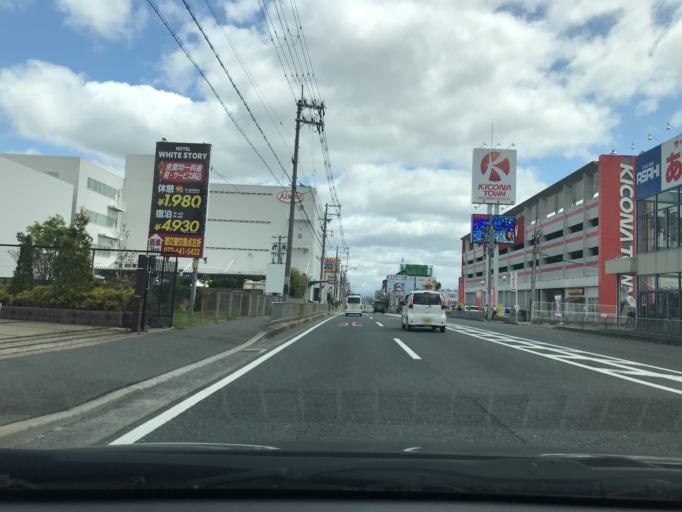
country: JP
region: Osaka
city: Ibaraki
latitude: 34.8362
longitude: 135.5288
